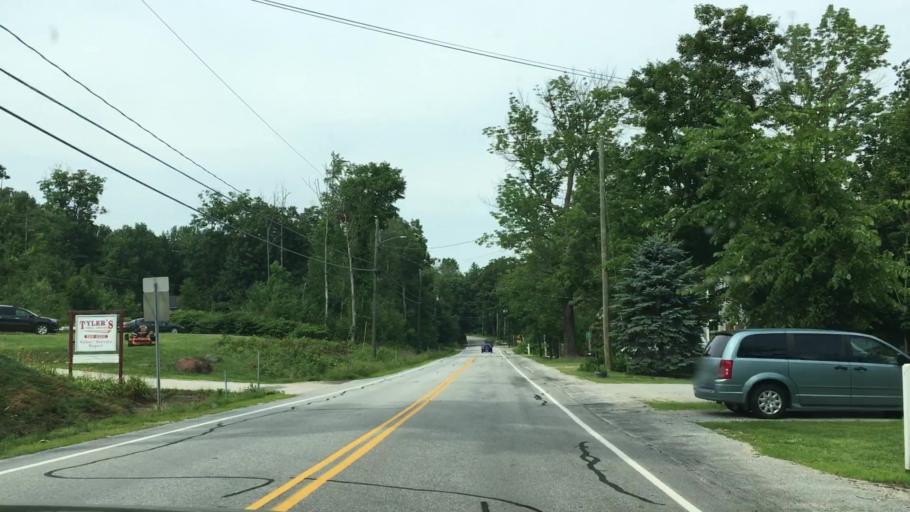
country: US
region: New Hampshire
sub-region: Hillsborough County
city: Antrim
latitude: 43.0335
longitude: -71.9369
